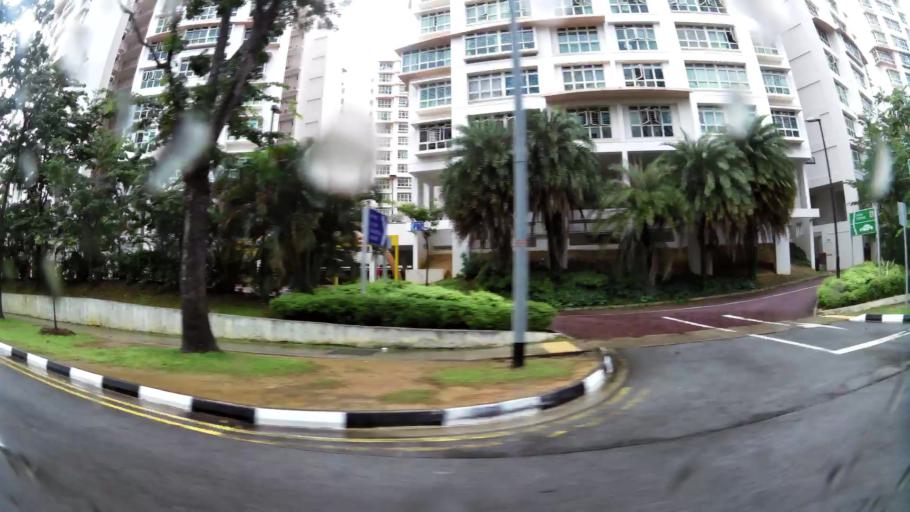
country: MY
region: Johor
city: Kampung Pasir Gudang Baru
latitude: 1.3865
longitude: 103.9008
